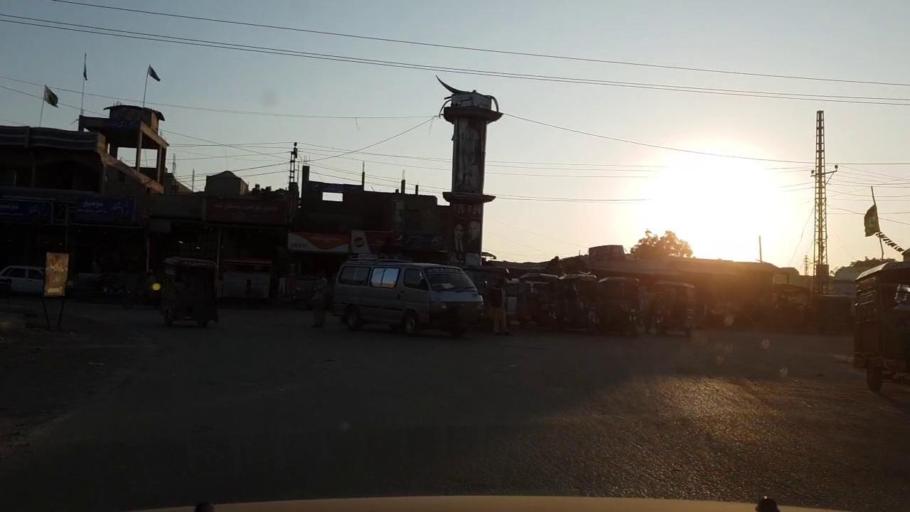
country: PK
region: Sindh
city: Thatta
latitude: 24.6056
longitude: 68.0705
